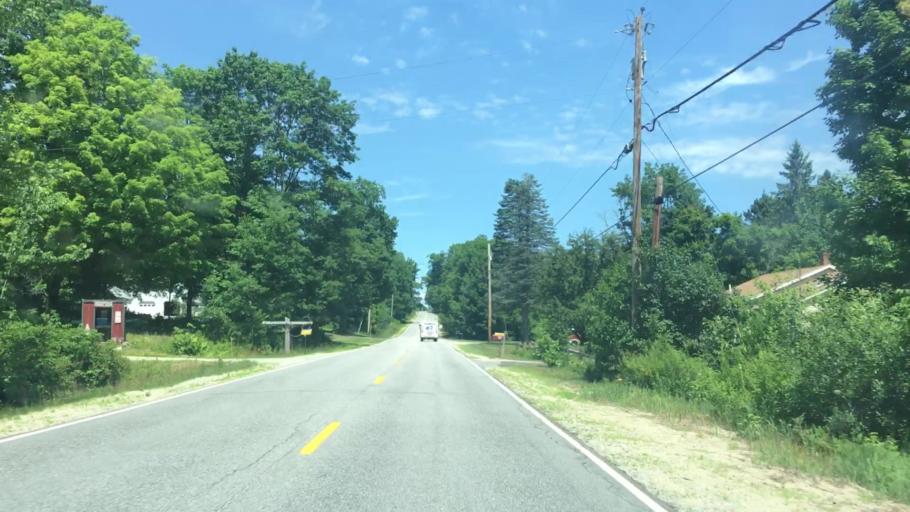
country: US
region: Maine
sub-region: Androscoggin County
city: Livermore
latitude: 44.3645
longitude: -70.2052
